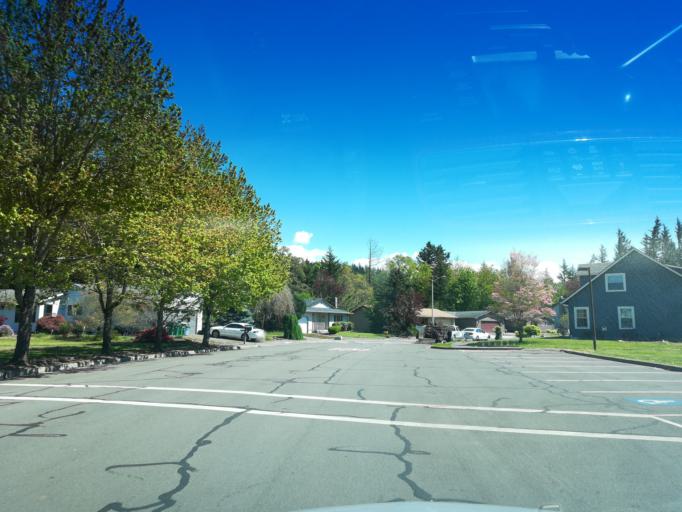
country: US
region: Oregon
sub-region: Multnomah County
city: Troutdale
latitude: 45.5291
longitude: -122.3754
